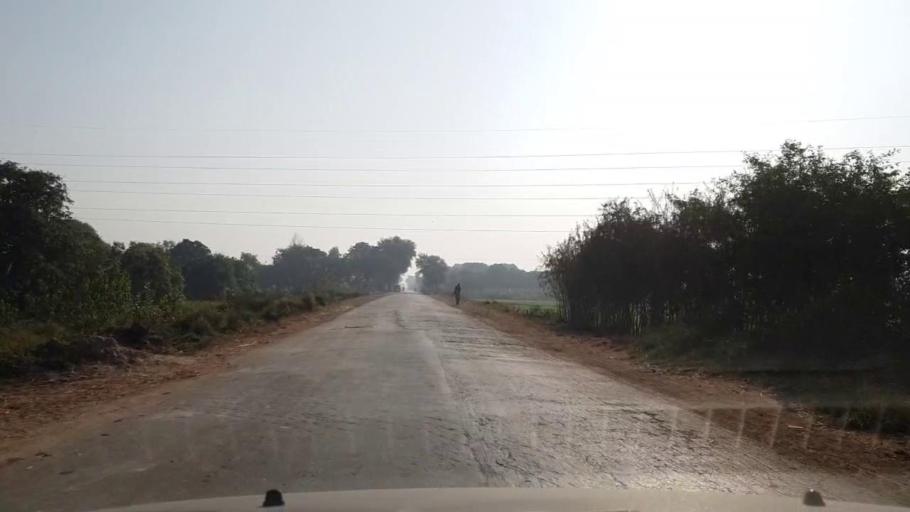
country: PK
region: Sindh
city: Matiari
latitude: 25.5981
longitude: 68.4589
